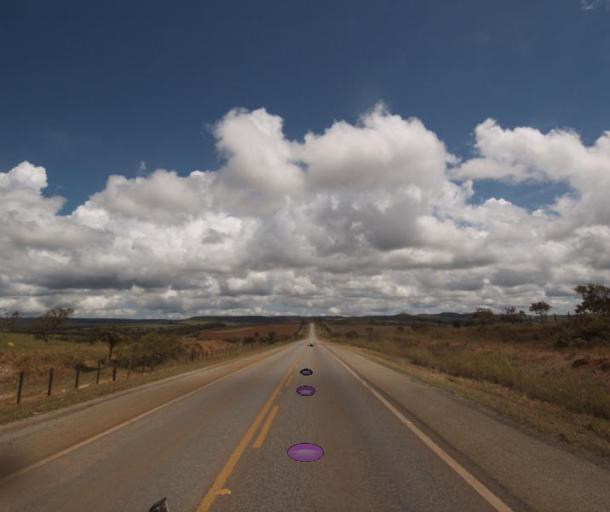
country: BR
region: Goias
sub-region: Pirenopolis
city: Pirenopolis
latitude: -15.7562
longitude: -48.6843
